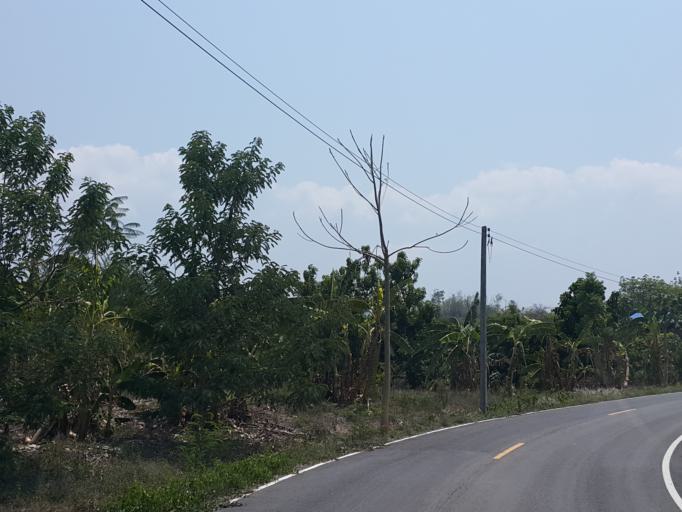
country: TH
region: Kanchanaburi
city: Sai Yok
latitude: 14.1838
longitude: 98.9581
